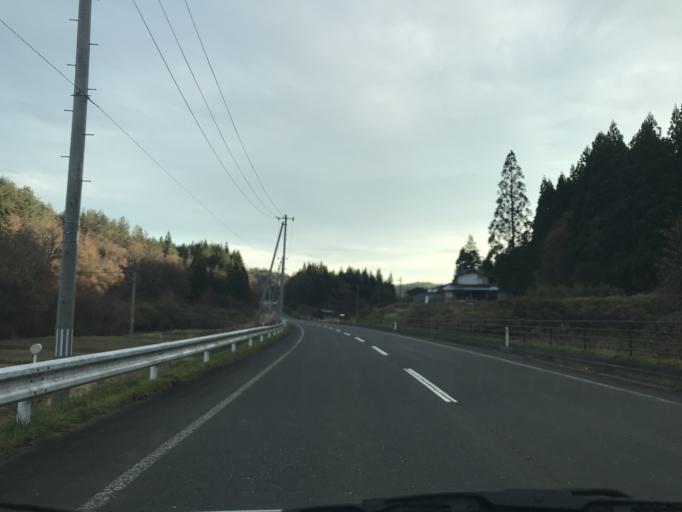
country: JP
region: Iwate
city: Ichinoseki
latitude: 38.9914
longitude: 141.0662
